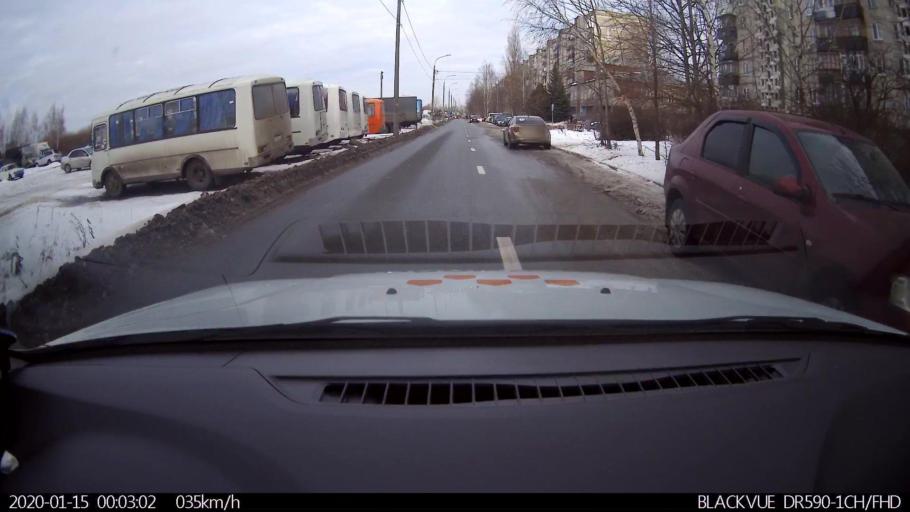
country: RU
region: Nizjnij Novgorod
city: Gorbatovka
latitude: 56.2716
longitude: 43.8747
